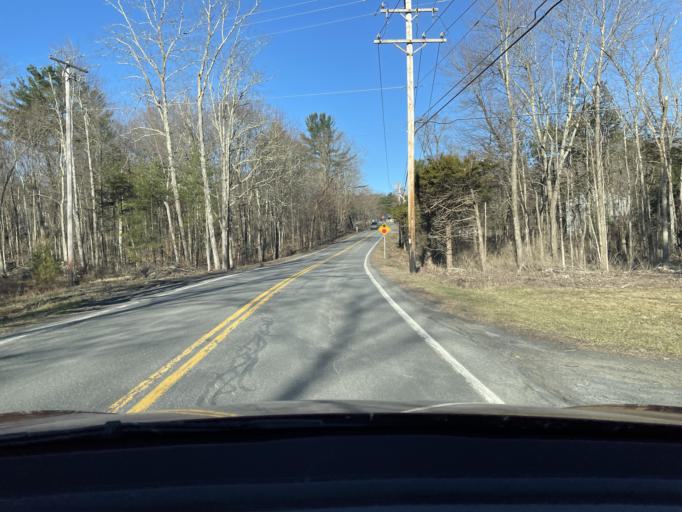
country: US
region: New York
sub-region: Ulster County
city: Zena
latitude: 42.0498
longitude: -74.0661
